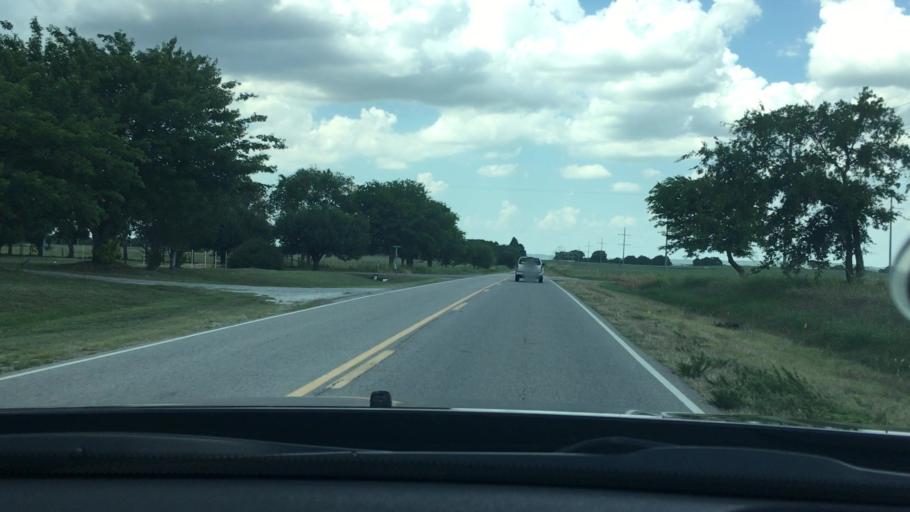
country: US
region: Oklahoma
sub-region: Pontotoc County
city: Ada
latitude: 34.6646
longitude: -96.6349
